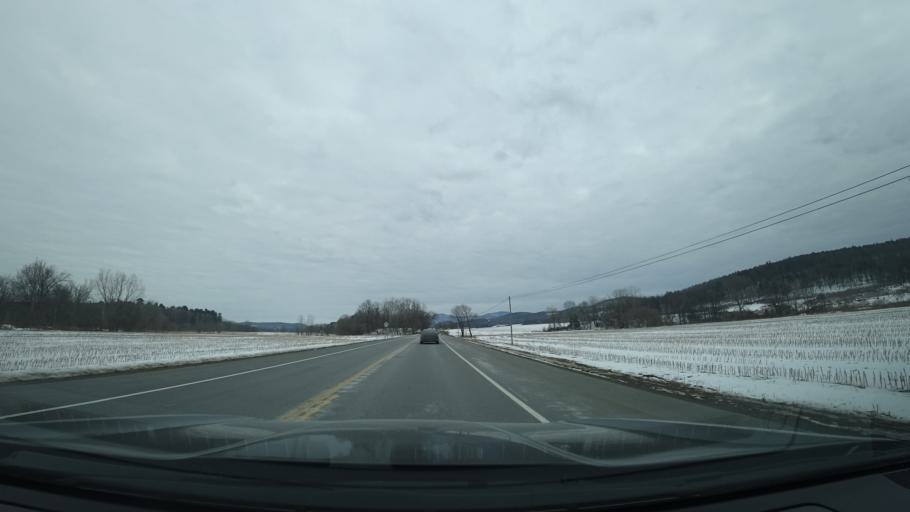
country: US
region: New York
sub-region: Washington County
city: Cambridge
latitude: 43.1526
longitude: -73.3490
